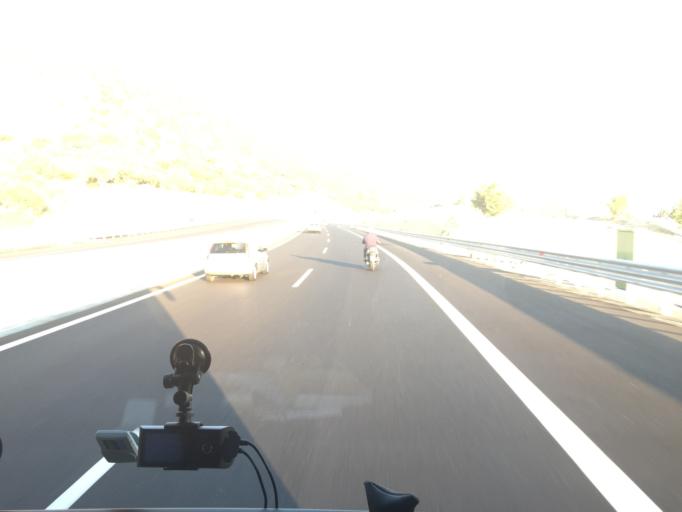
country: GR
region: Peloponnese
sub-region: Nomos Korinthias
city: Xylokastro
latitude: 38.0847
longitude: 22.5868
